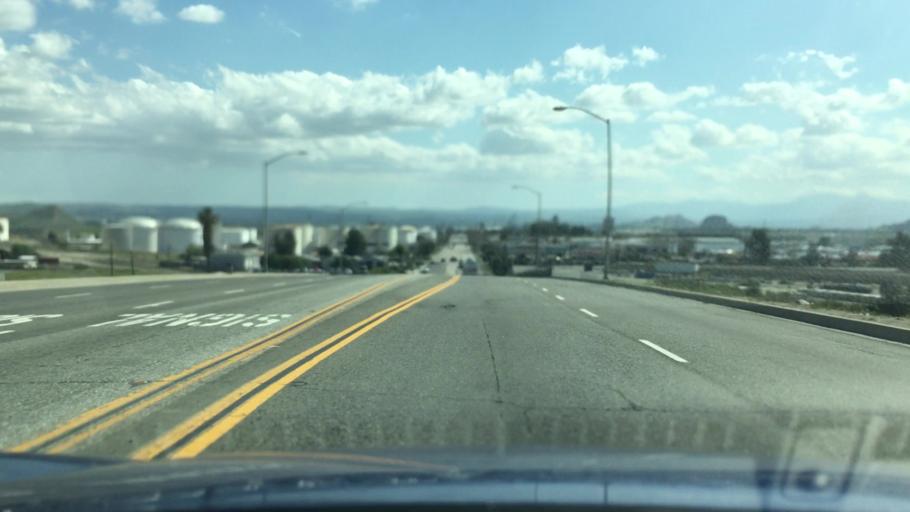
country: US
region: California
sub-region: San Bernardino County
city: Bloomington
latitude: 34.0668
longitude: -117.3703
